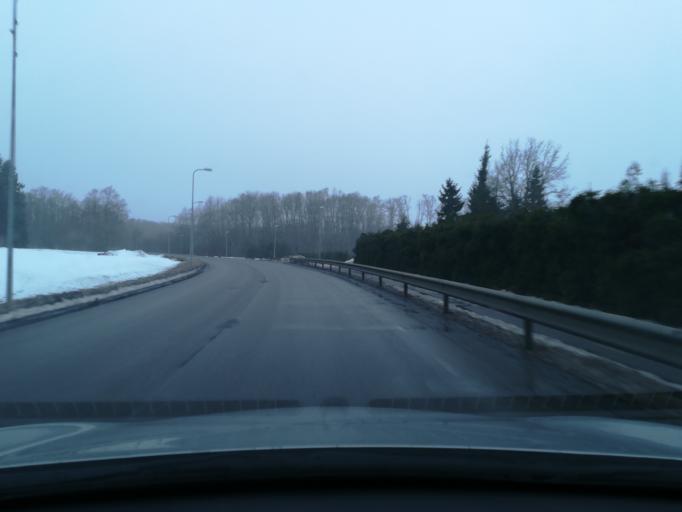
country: EE
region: Harju
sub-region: Rae vald
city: Jueri
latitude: 59.3626
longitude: 24.9456
